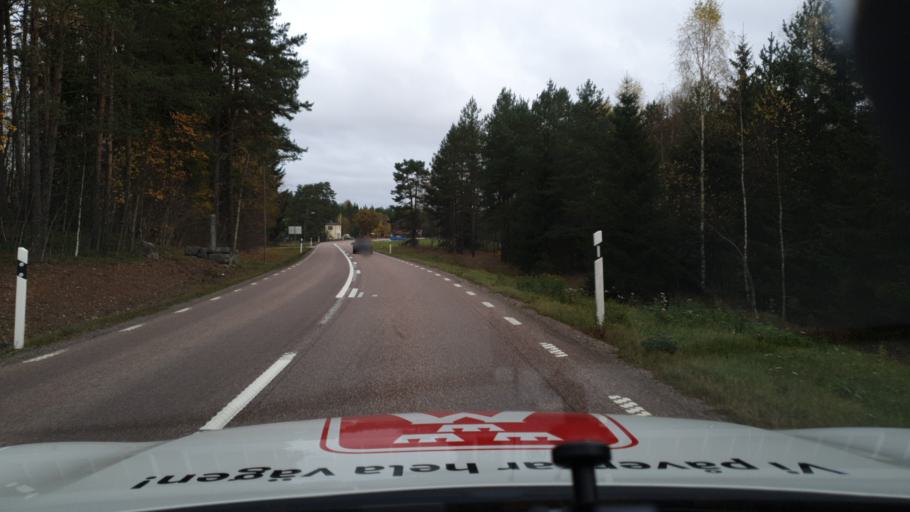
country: SE
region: Gaevleborg
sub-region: Gavle Kommun
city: Hedesunda
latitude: 60.4980
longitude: 16.9385
